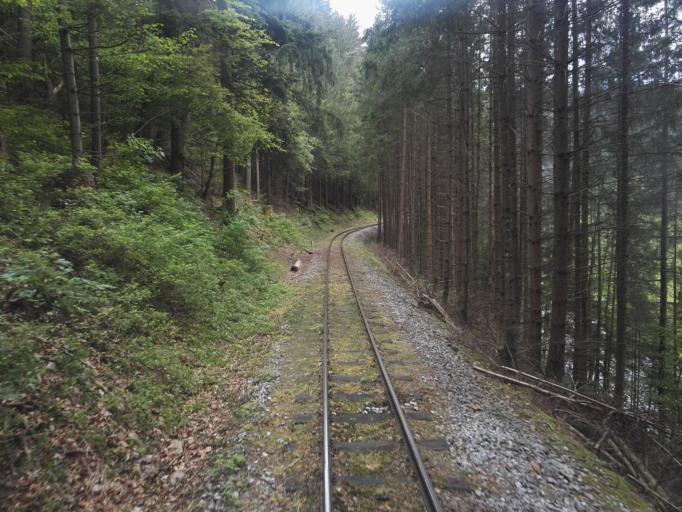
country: AT
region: Styria
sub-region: Politischer Bezirk Weiz
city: Koglhof
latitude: 47.3323
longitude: 15.6975
